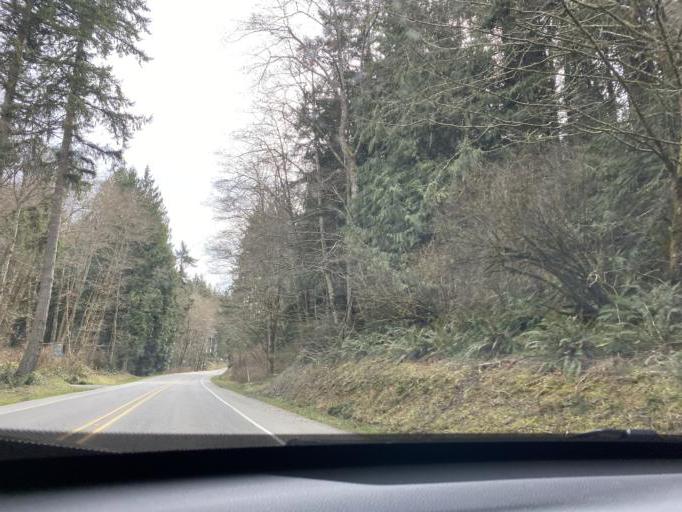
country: US
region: Washington
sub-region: Island County
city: Langley
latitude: 48.0213
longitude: -122.4091
